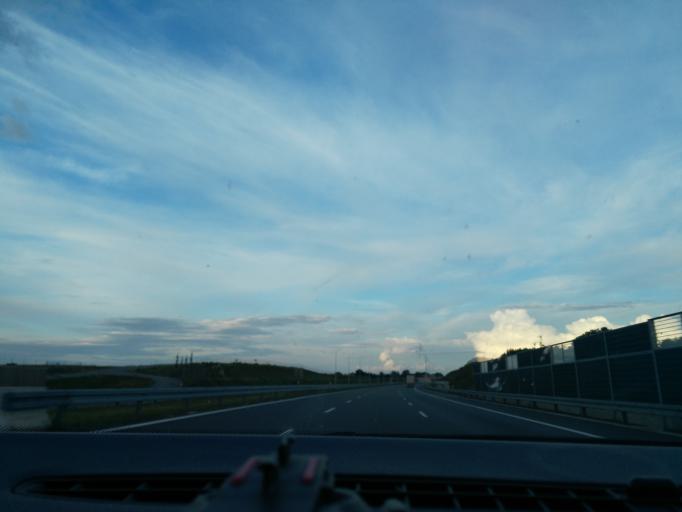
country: PL
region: Lublin Voivodeship
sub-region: Powiat lubelski
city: Jastkow
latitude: 51.3017
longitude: 22.5054
